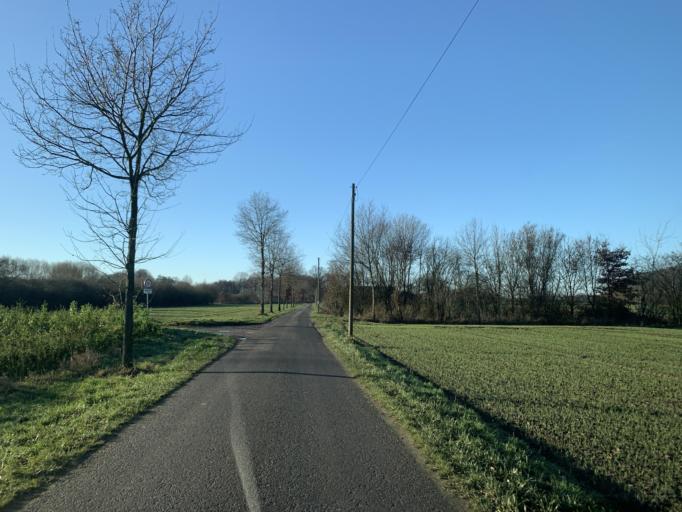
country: DE
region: North Rhine-Westphalia
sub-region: Regierungsbezirk Munster
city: Dulmen
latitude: 51.8771
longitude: 7.2743
